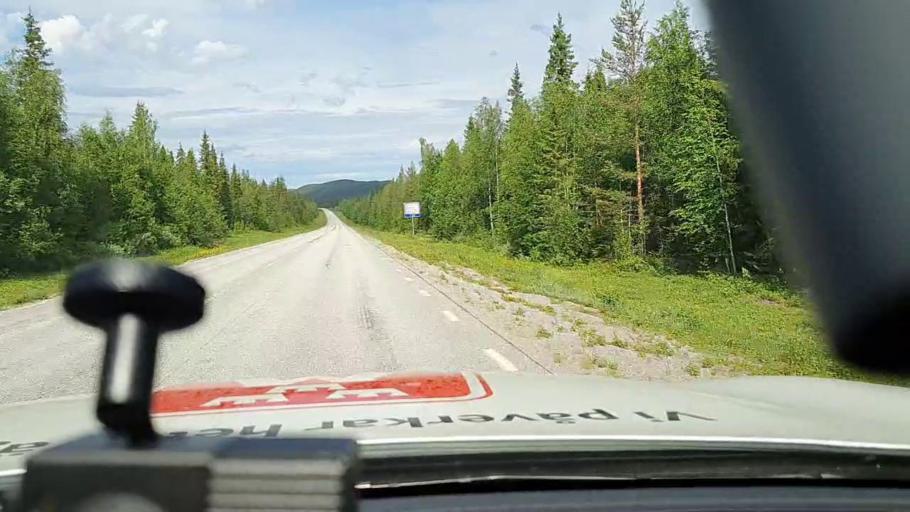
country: SE
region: Norrbotten
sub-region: Jokkmokks Kommun
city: Jokkmokk
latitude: 66.5462
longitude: 20.1327
